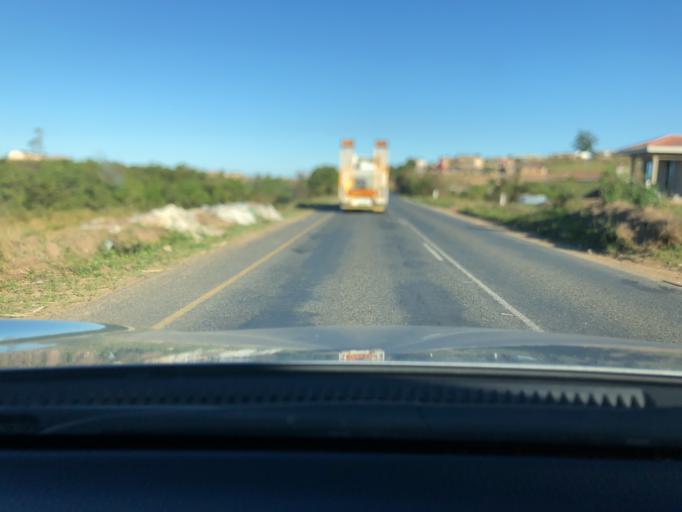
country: ZA
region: KwaZulu-Natal
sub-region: eThekwini Metropolitan Municipality
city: Umkomaas
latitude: -30.0007
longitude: 30.7998
